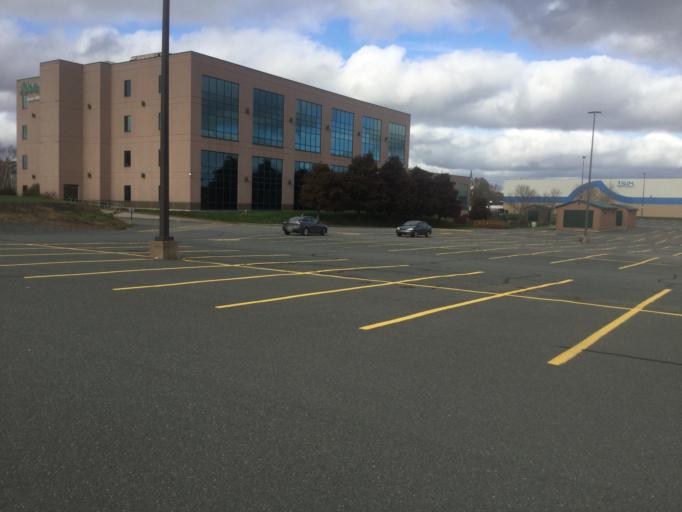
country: CA
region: Nova Scotia
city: New Glasgow
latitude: 45.5712
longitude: -62.6570
